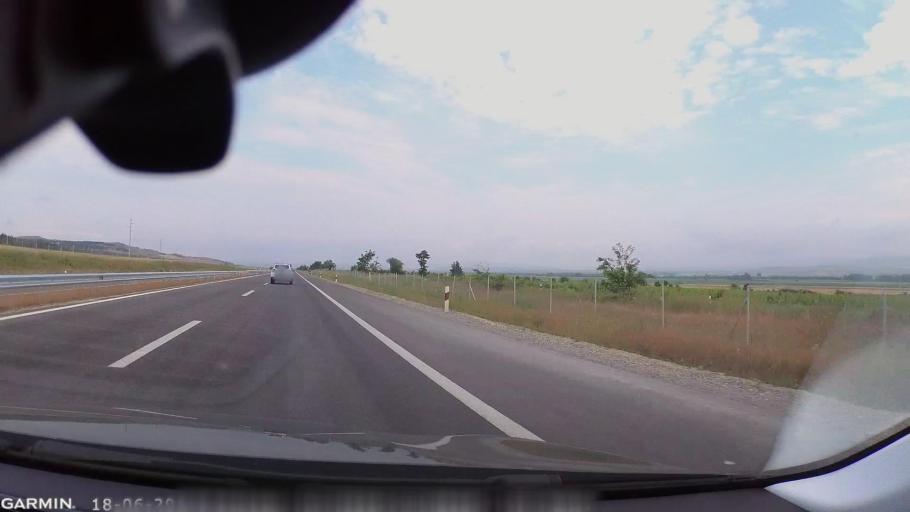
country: MK
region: Stip
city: Shtip
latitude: 41.7933
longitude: 22.0961
